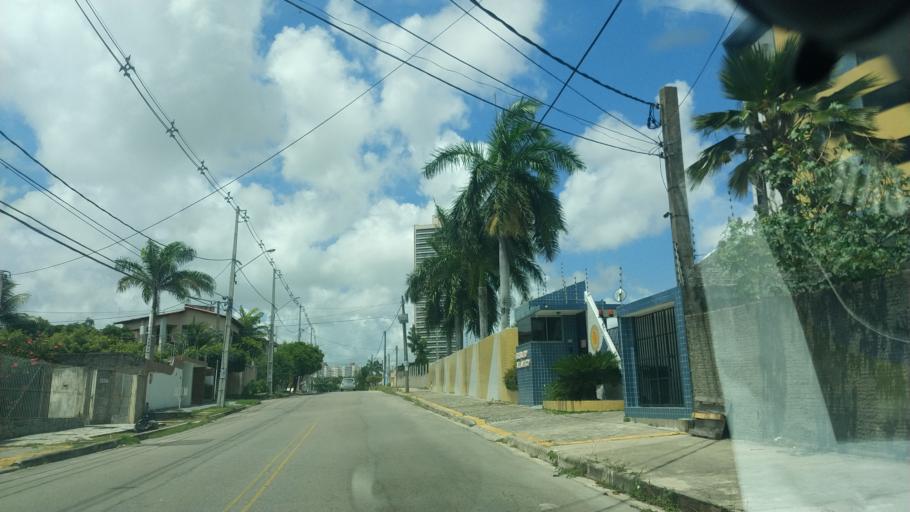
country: BR
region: Rio Grande do Norte
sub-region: Natal
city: Natal
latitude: -5.8674
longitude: -35.1915
